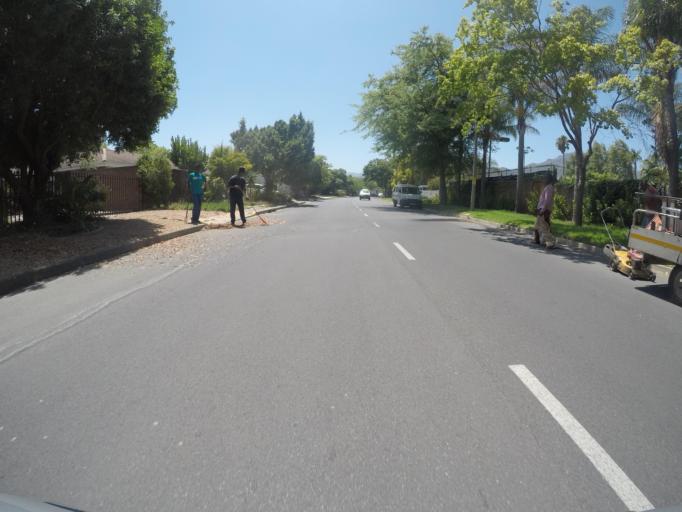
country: ZA
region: Western Cape
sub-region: Cape Winelands District Municipality
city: Stellenbosch
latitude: -33.9454
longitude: 18.8474
